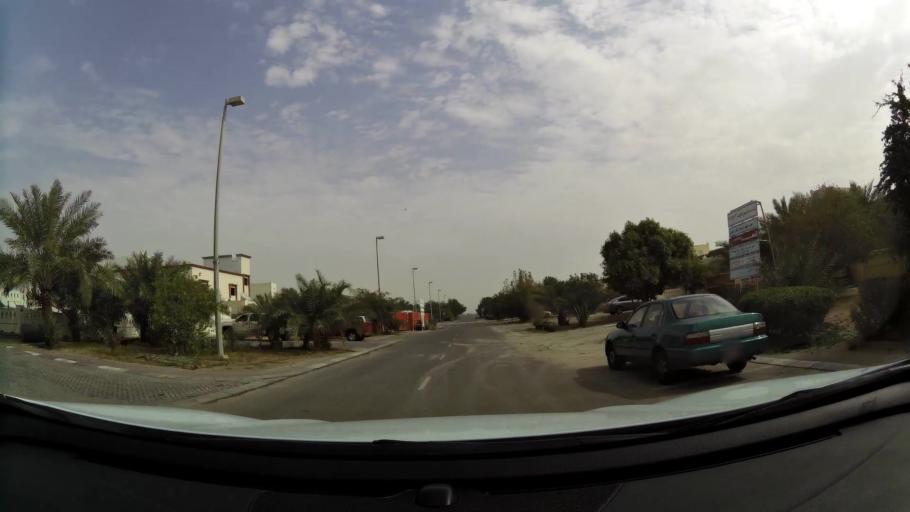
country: AE
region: Abu Dhabi
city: Abu Dhabi
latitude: 24.2986
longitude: 54.6607
